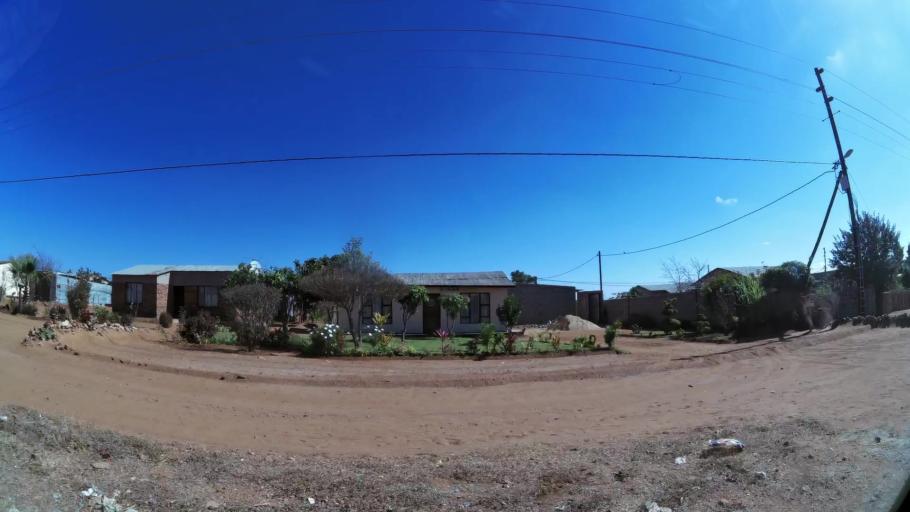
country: ZA
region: Limpopo
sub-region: Capricorn District Municipality
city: Polokwane
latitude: -23.8768
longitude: 29.4102
